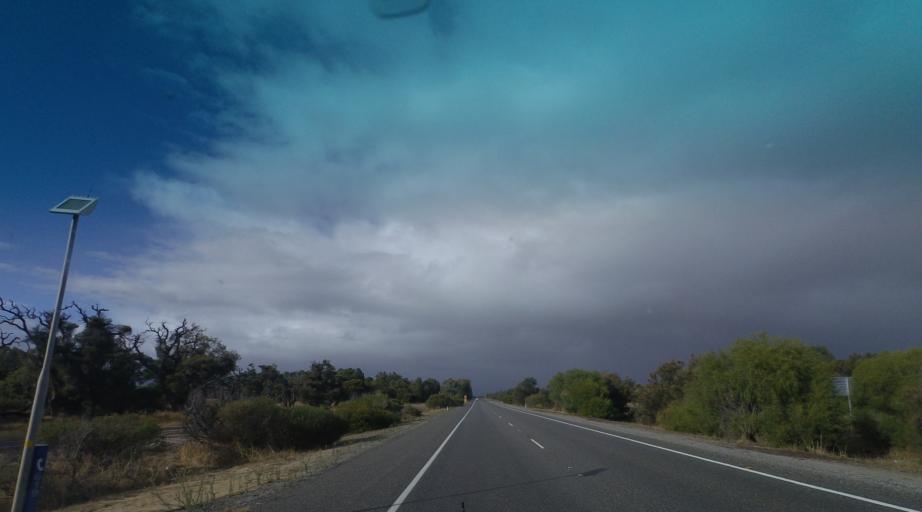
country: AU
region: Western Australia
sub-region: Serpentine-Jarrahdale
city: Oakford
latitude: -32.1887
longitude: 115.9625
